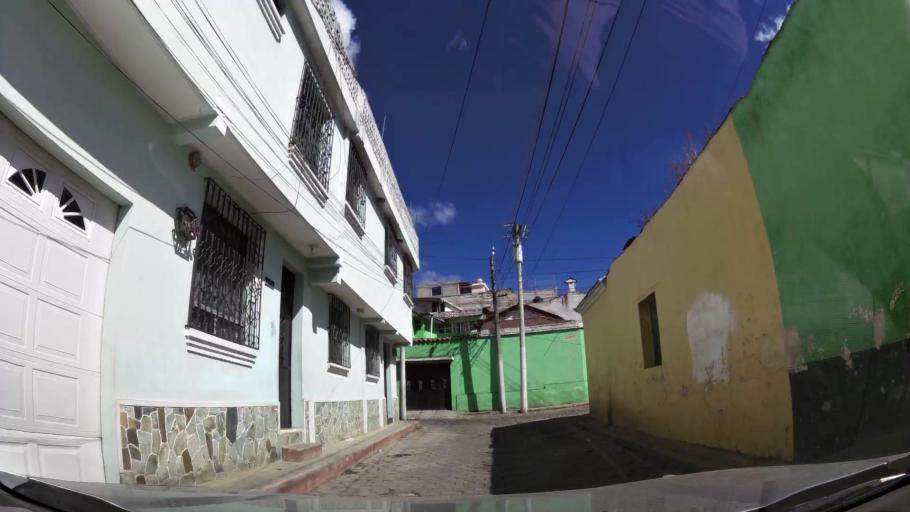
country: GT
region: Quetzaltenango
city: Quetzaltenango
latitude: 14.8354
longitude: -91.5156
